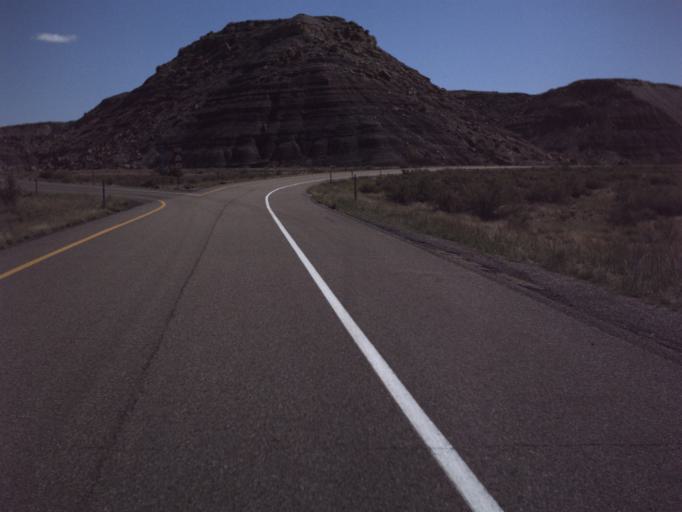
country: US
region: Utah
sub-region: Carbon County
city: East Carbon City
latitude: 38.9206
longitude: -110.3776
